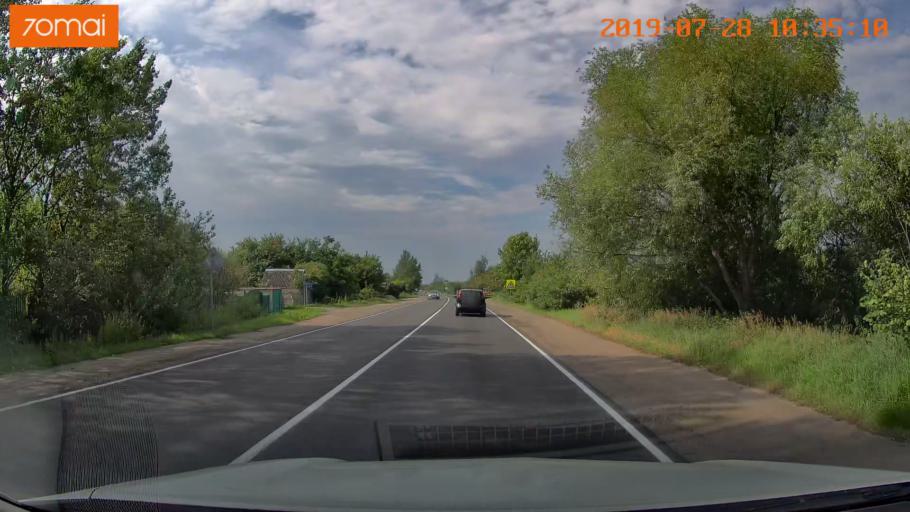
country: RU
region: Kaliningrad
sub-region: Gorod Kaliningrad
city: Kaliningrad
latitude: 54.7492
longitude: 20.4341
